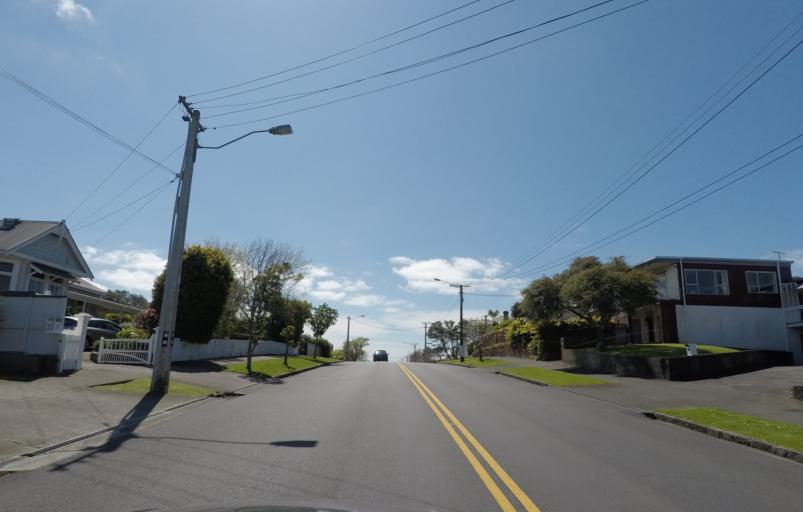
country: NZ
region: Auckland
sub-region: Auckland
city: Auckland
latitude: -36.8843
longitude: 174.8091
